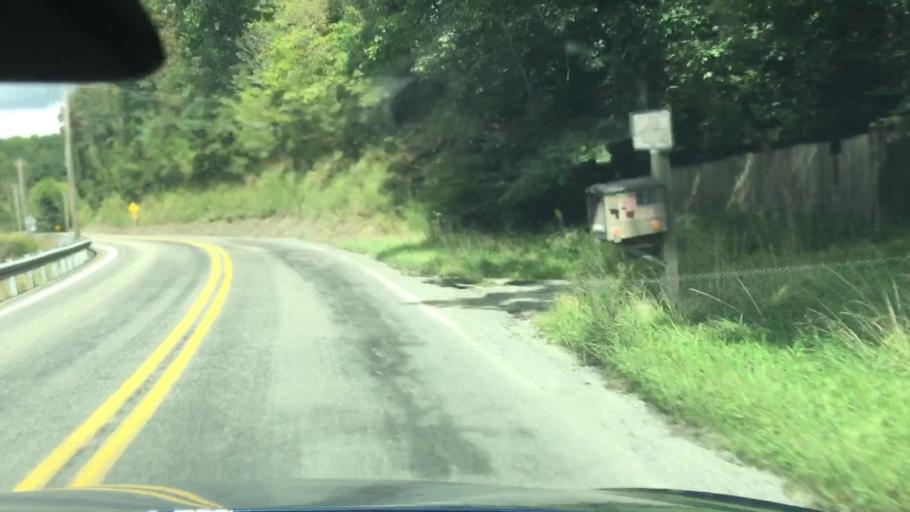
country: US
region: Pennsylvania
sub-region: Allegheny County
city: Curtisville
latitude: 40.6419
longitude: -79.8396
